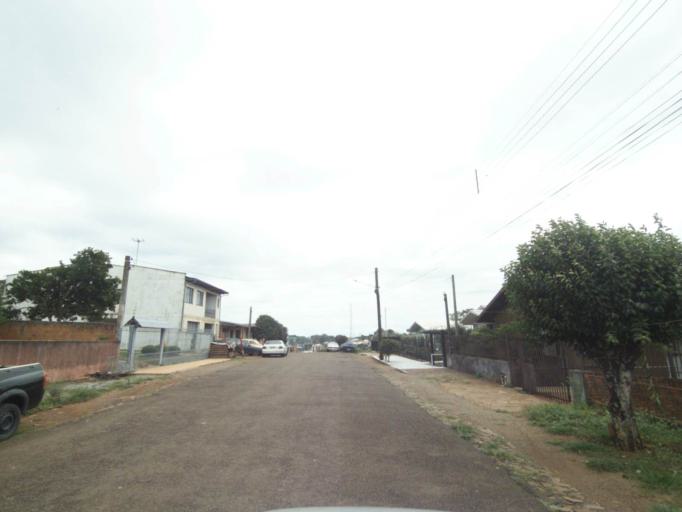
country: BR
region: Rio Grande do Sul
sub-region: Lagoa Vermelha
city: Lagoa Vermelha
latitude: -28.2132
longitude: -51.5337
